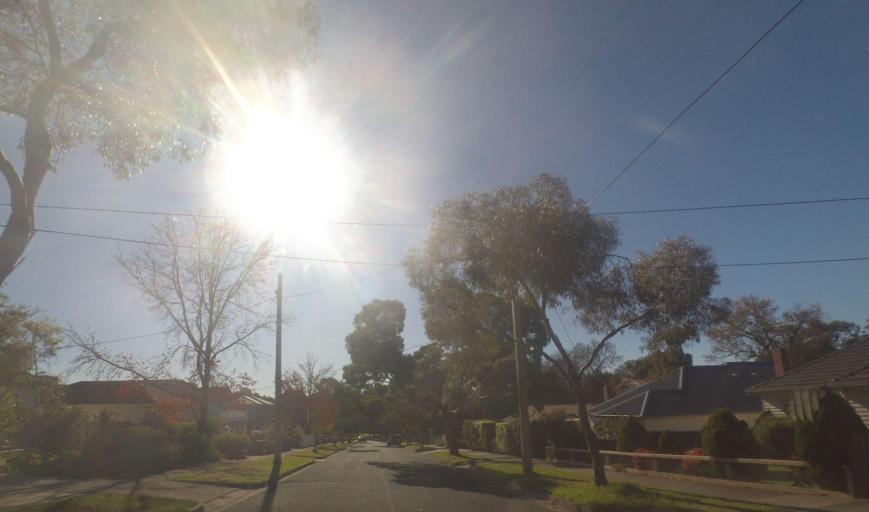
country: AU
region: Victoria
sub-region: Whitehorse
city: Box Hill North
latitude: -37.8043
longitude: 145.1232
